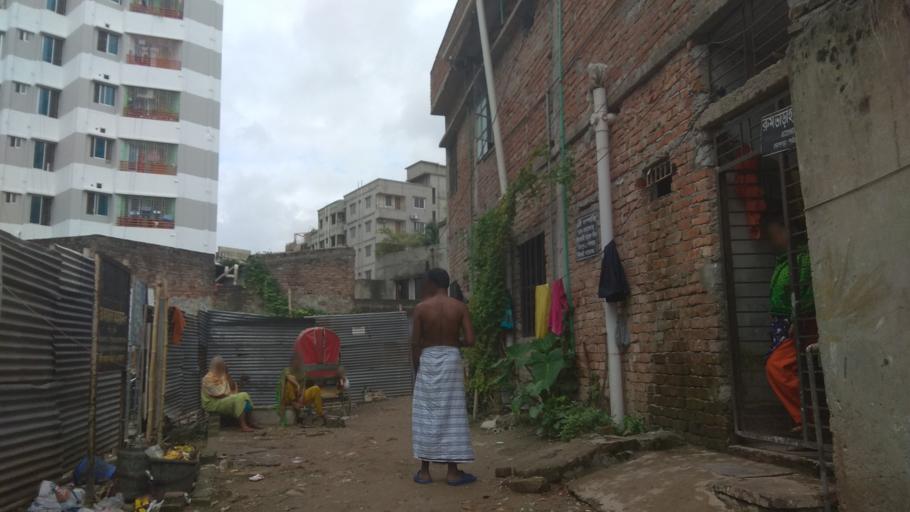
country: BD
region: Dhaka
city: Azimpur
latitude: 23.8022
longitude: 90.3749
